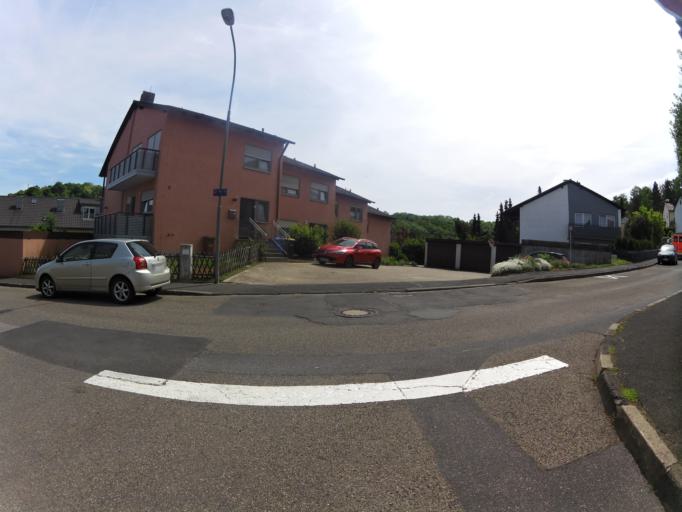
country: DE
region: Bavaria
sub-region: Regierungsbezirk Unterfranken
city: Ochsenfurt
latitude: 49.6674
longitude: 10.0421
